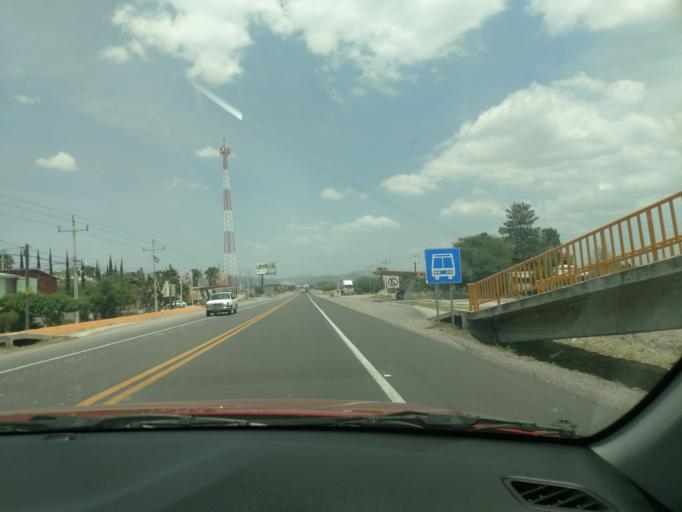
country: MX
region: San Luis Potosi
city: Rio Verde
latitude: 21.9185
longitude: -99.9517
